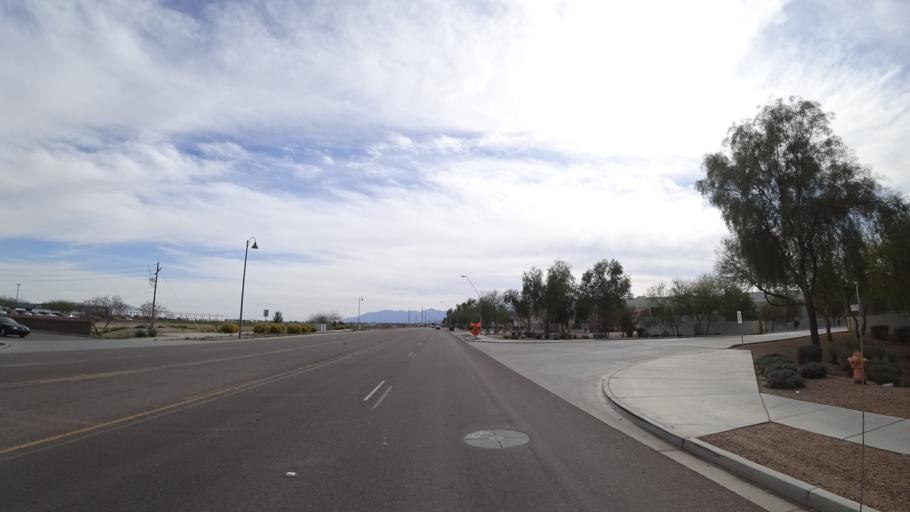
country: US
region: Arizona
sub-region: Maricopa County
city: Tolleson
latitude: 33.4402
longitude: -112.2552
